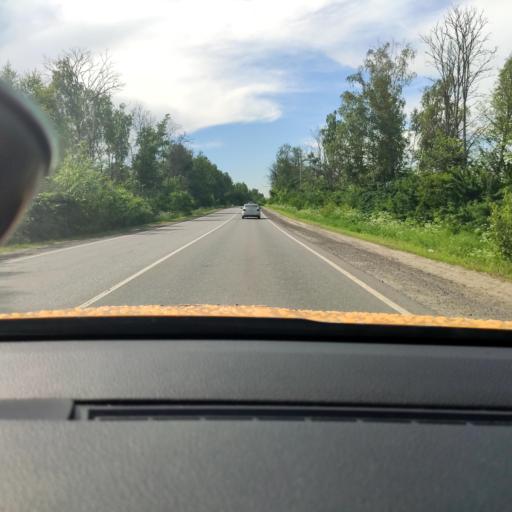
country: RU
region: Moskovskaya
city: Zhilevo
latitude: 54.9589
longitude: 37.9940
